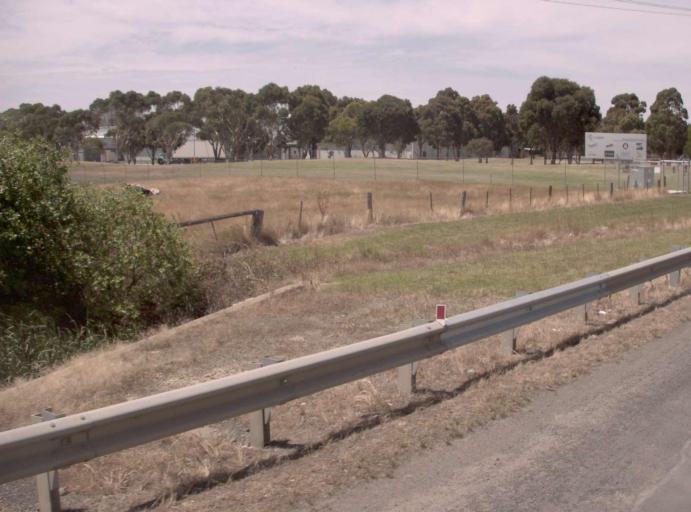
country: AU
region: Victoria
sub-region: Latrobe
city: Morwell
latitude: -38.2316
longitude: 146.4500
